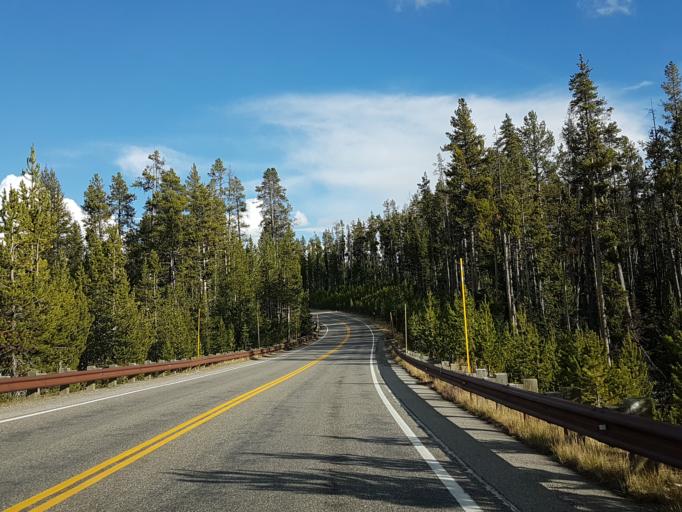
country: US
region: Montana
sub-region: Gallatin County
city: West Yellowstone
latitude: 44.4475
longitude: -110.7031
